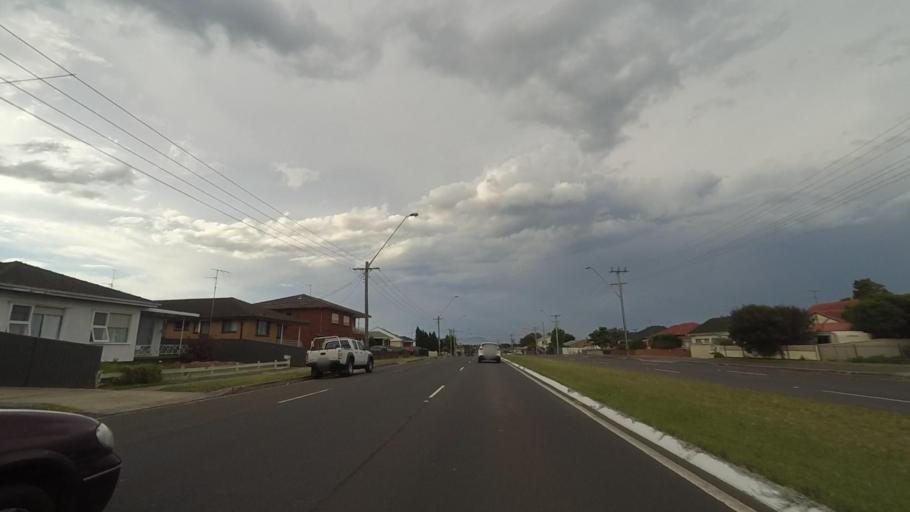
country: AU
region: New South Wales
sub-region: Shellharbour
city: Barrack Heights
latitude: -34.5634
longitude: 150.8601
